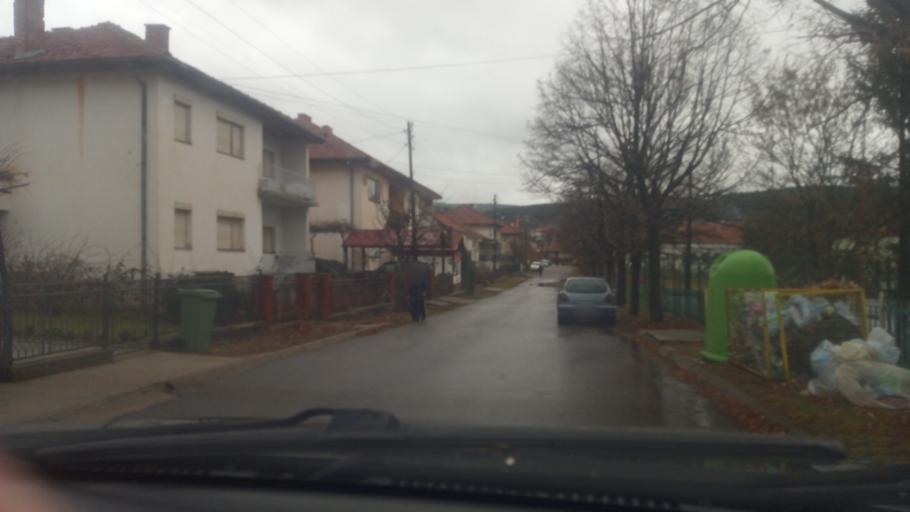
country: MK
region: Pehcevo
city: Pehcevo
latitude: 41.7631
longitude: 22.8830
